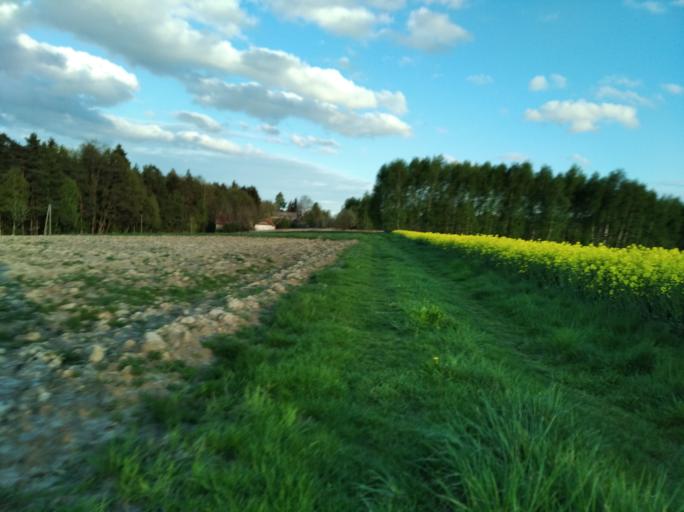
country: PL
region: Subcarpathian Voivodeship
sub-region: Powiat strzyzowski
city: Wysoka Strzyzowska
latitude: 49.8574
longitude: 21.7606
